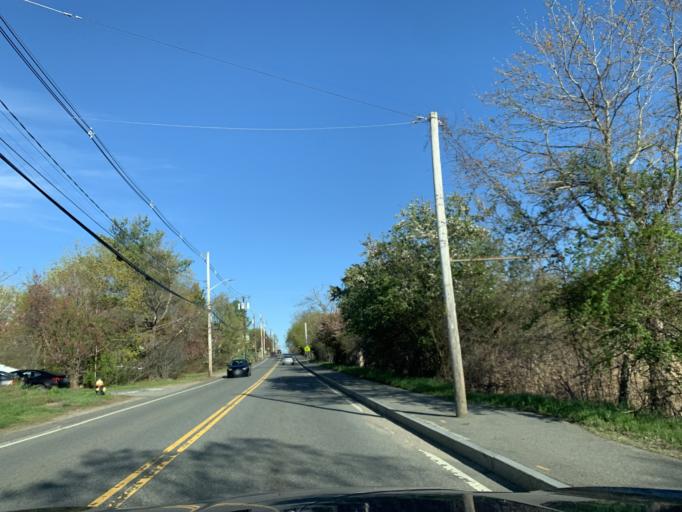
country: US
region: Massachusetts
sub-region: Norfolk County
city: Stoughton
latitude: 42.1285
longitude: -71.1178
